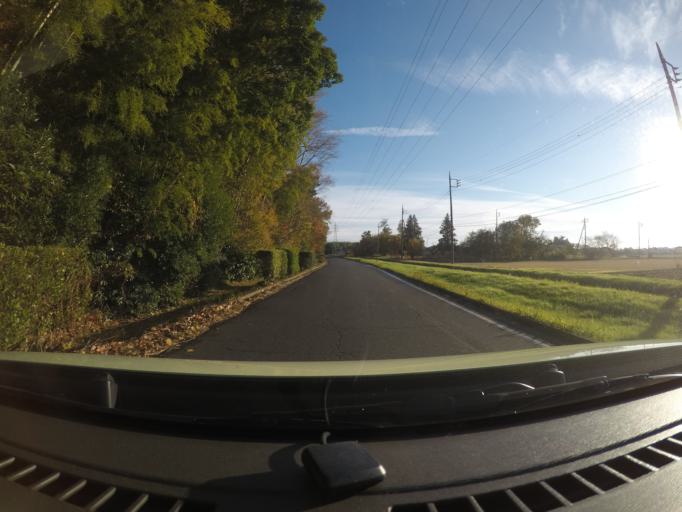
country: JP
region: Ibaraki
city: Tsukuba
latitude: 36.1170
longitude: 140.0919
